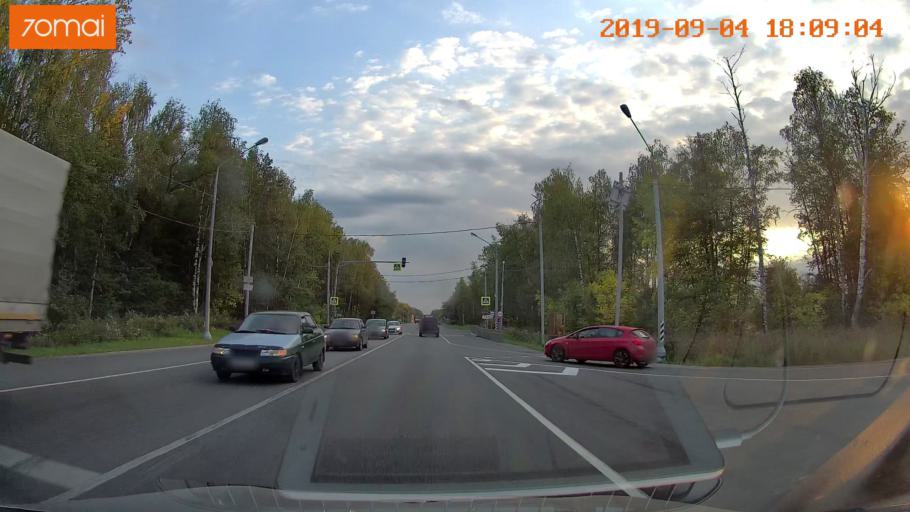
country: RU
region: Moskovskaya
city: Khorlovo
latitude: 55.3991
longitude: 38.7782
